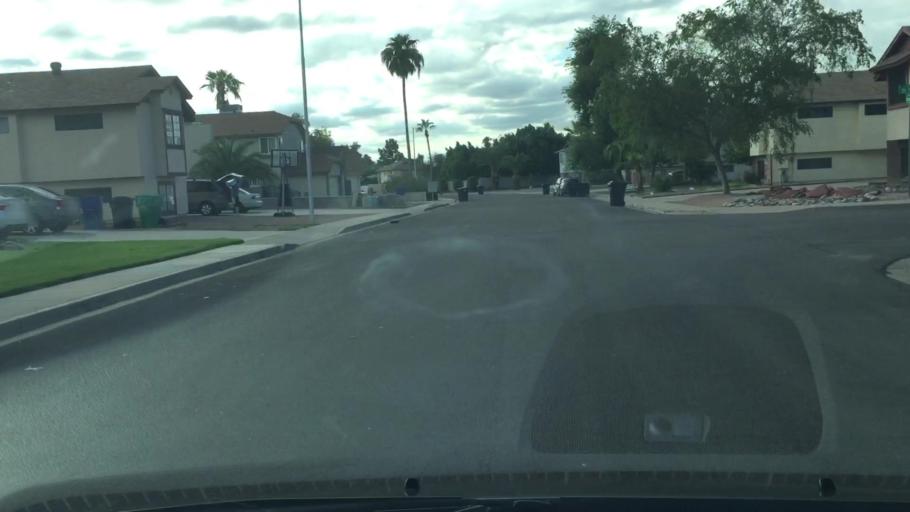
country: US
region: Arizona
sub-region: Maricopa County
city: Mesa
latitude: 33.4294
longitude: -111.7222
